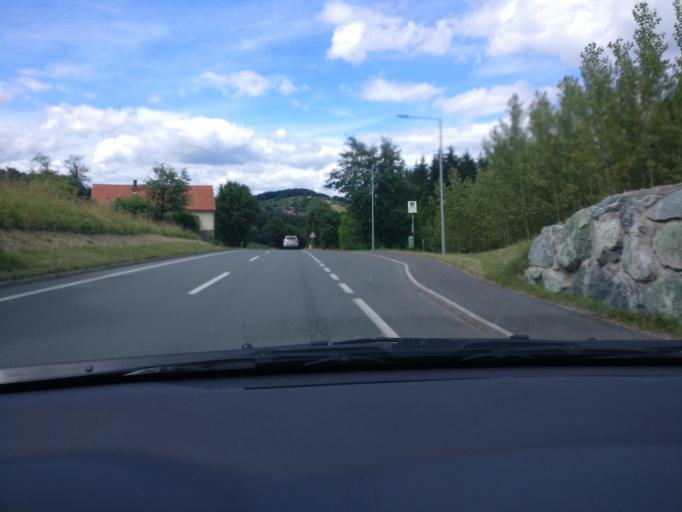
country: AT
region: Styria
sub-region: Politischer Bezirk Weiz
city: Hirnsdorf
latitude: 47.1865
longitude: 15.8146
